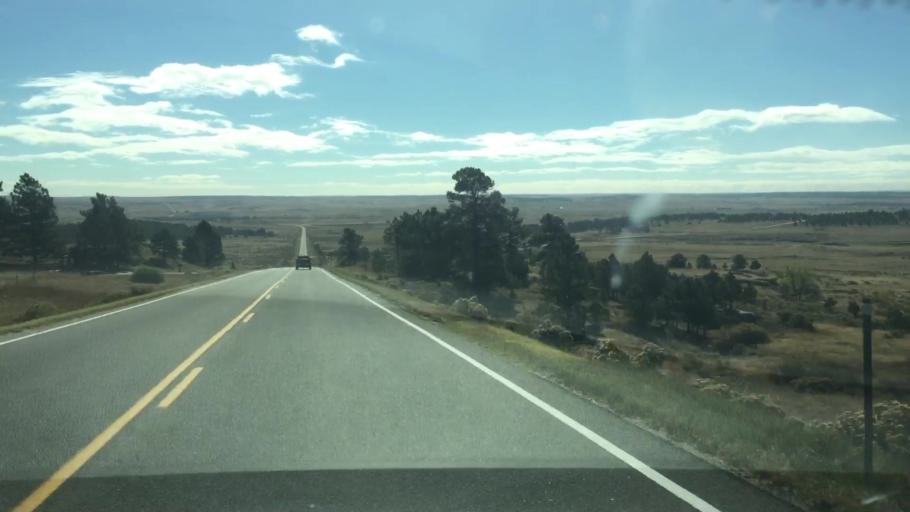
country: US
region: Colorado
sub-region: Elbert County
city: Kiowa
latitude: 39.3130
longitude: -104.3656
